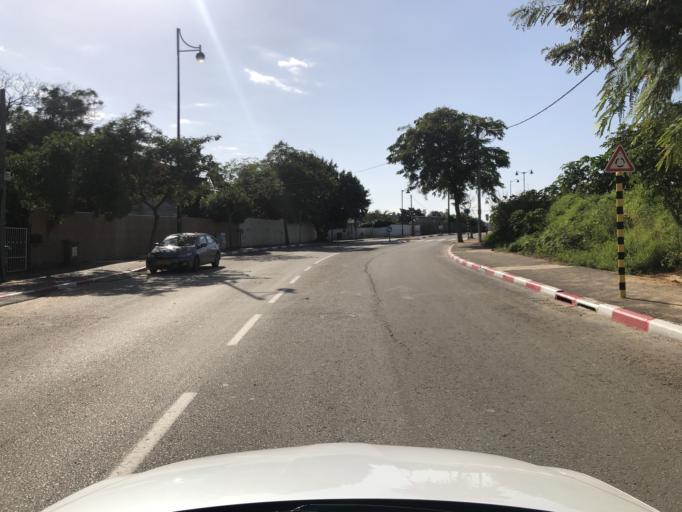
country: IL
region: Central District
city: Ness Ziona
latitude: 31.9103
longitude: 34.7905
